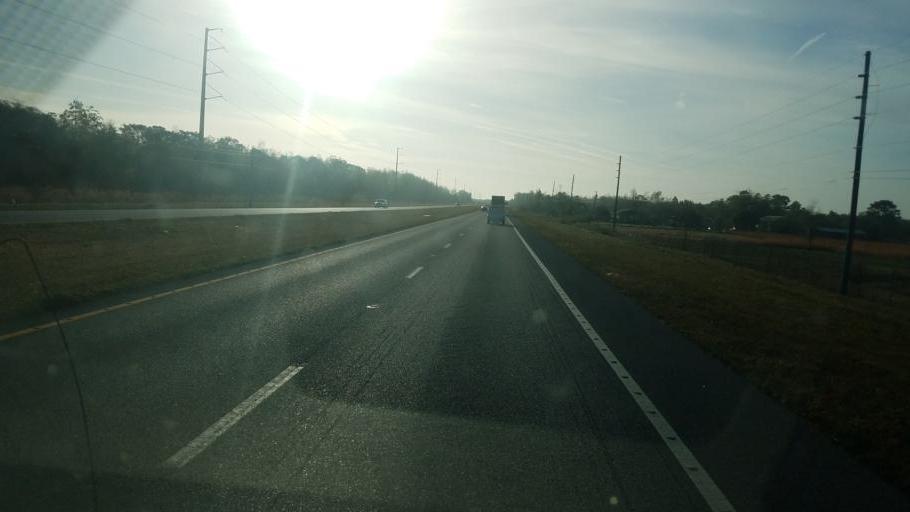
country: US
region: Florida
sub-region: Osceola County
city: Saint Cloud
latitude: 28.1635
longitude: -81.1202
